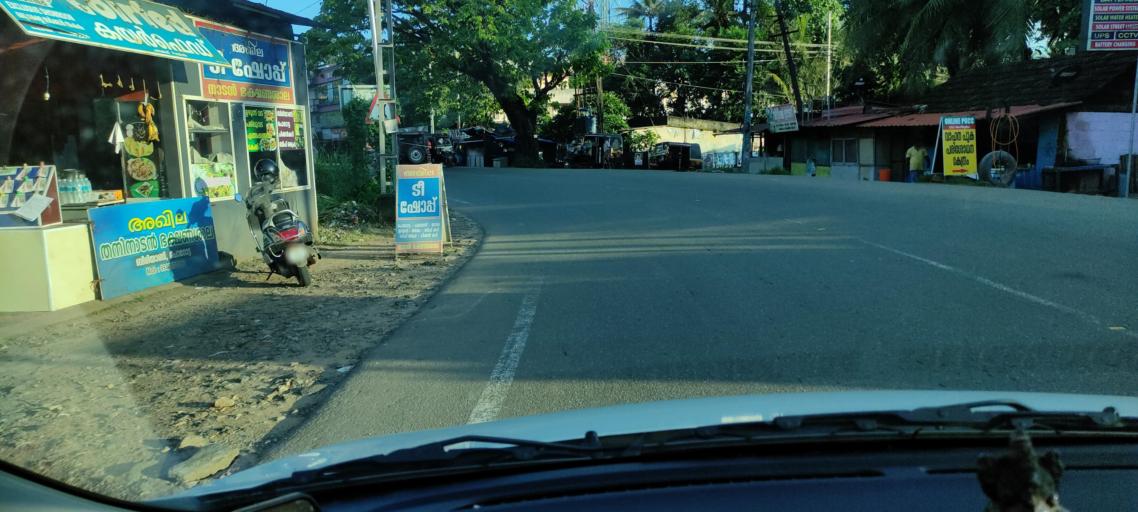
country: IN
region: Kerala
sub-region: Pattanamtitta
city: Adur
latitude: 9.1453
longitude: 76.7653
